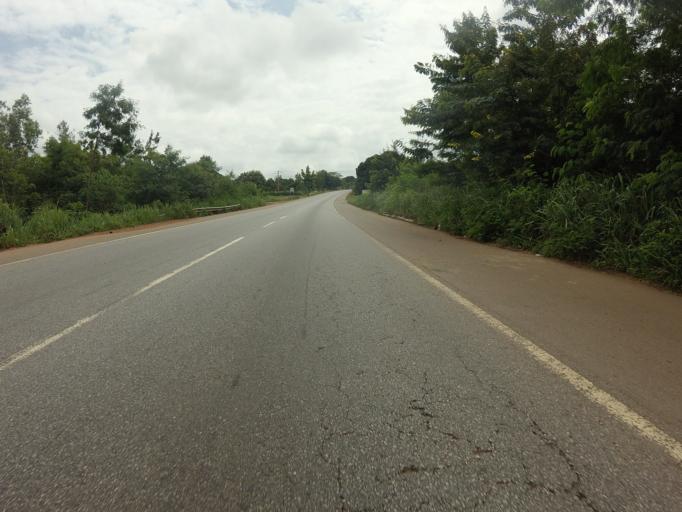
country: GH
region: Brong-Ahafo
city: Techiman
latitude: 7.4623
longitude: -1.9704
